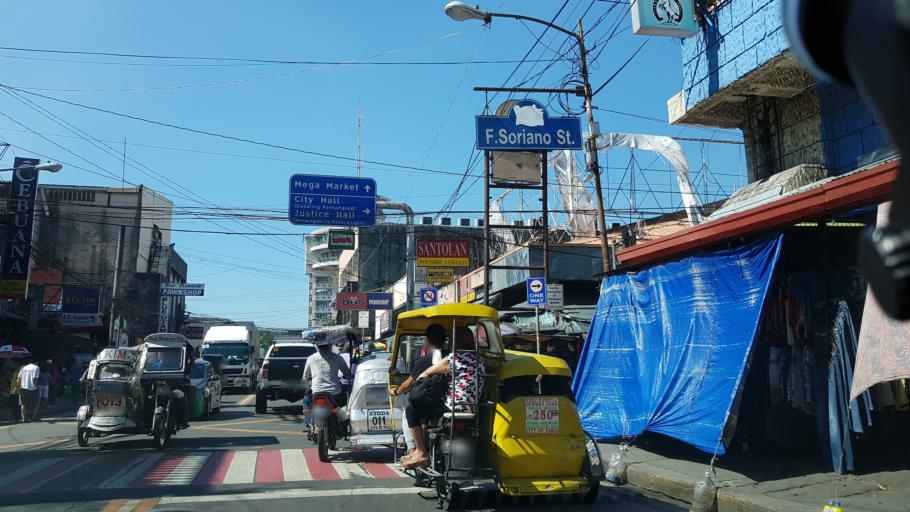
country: PH
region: Calabarzon
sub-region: Province of Rizal
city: Pateros
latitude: 14.5605
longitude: 121.0838
